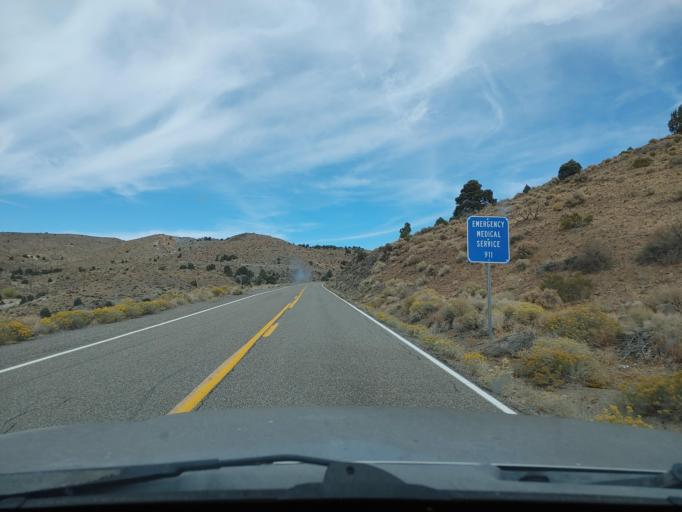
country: US
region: Nevada
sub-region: Storey County
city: Virginia City
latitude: 39.2767
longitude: -119.6288
